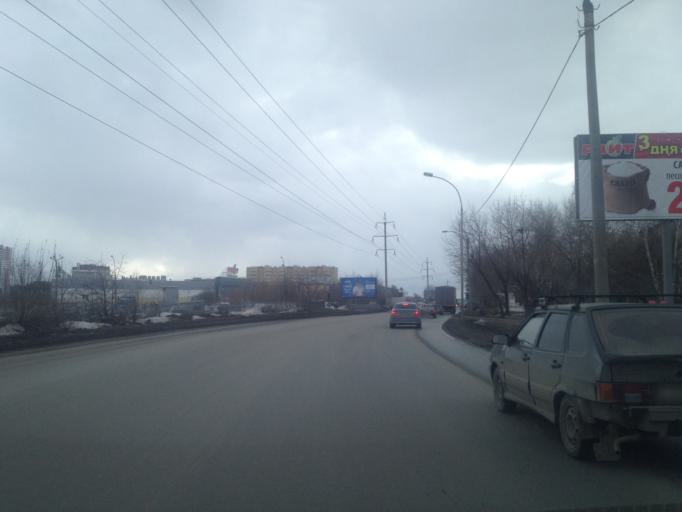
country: RU
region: Sverdlovsk
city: Sovkhoznyy
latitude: 56.7747
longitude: 60.5988
